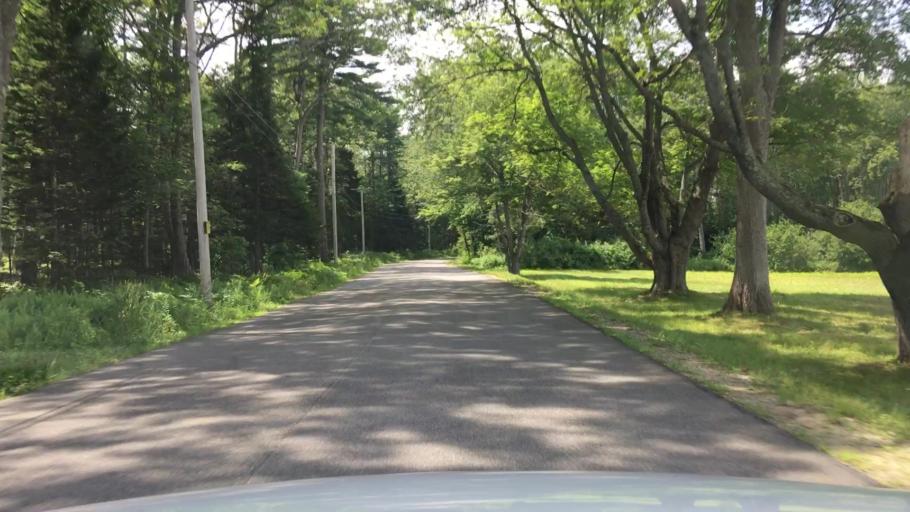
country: US
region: Maine
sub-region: Cumberland County
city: Scarborough
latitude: 43.5723
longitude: -70.2556
